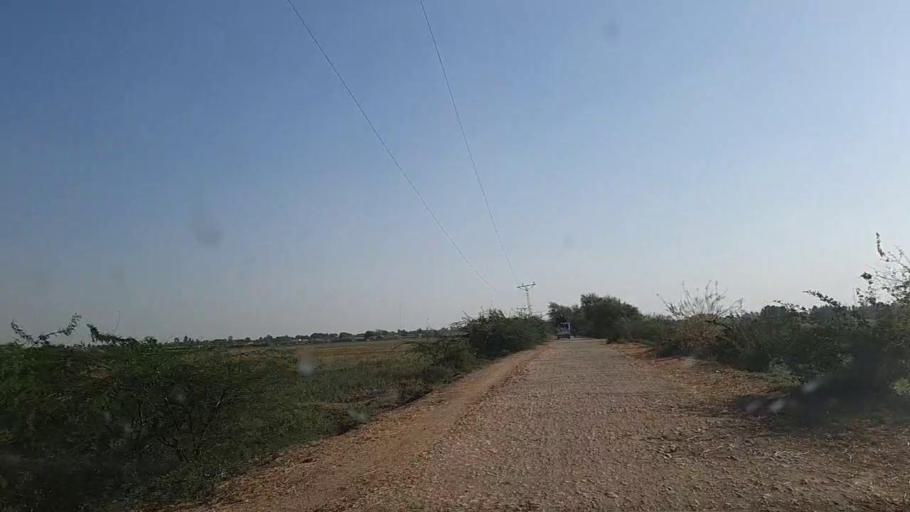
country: PK
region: Sindh
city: Thatta
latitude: 24.6177
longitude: 68.0781
